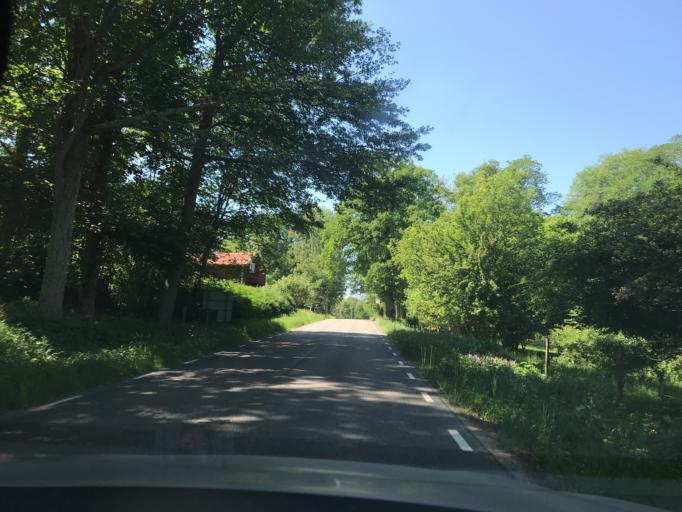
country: SE
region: Vaestra Goetaland
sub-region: Gotene Kommun
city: Goetene
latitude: 58.6225
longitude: 13.4154
